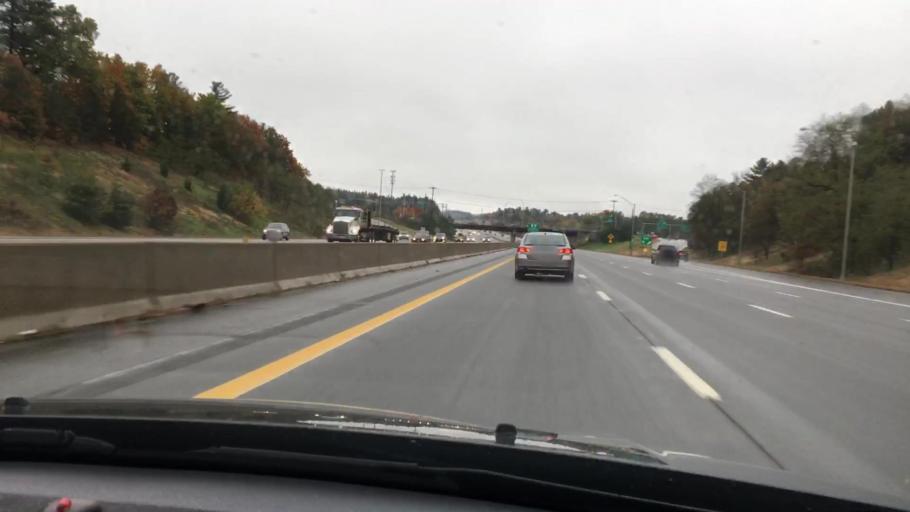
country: US
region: New Hampshire
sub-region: Hillsborough County
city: Nashua
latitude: 42.7724
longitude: -71.4932
